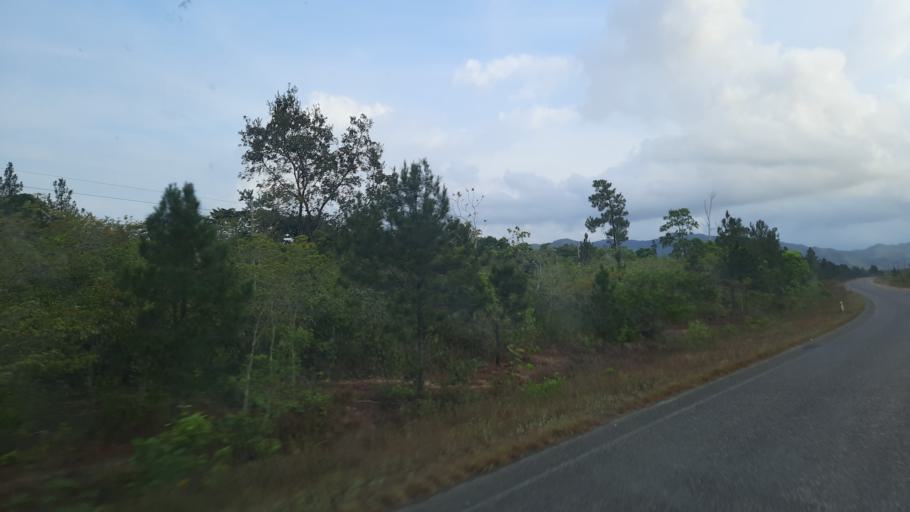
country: BZ
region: Stann Creek
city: Placencia
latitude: 16.6807
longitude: -88.4376
